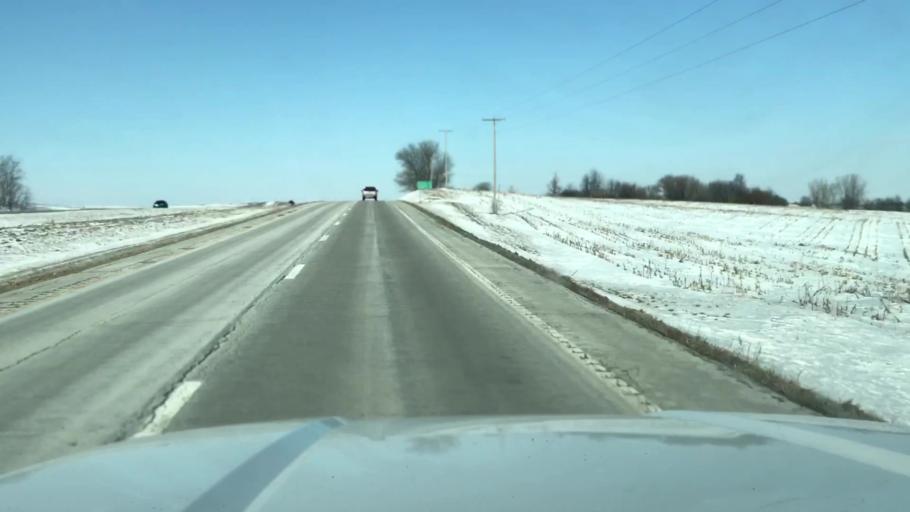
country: US
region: Missouri
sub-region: Andrew County
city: Savannah
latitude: 39.9679
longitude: -94.8680
